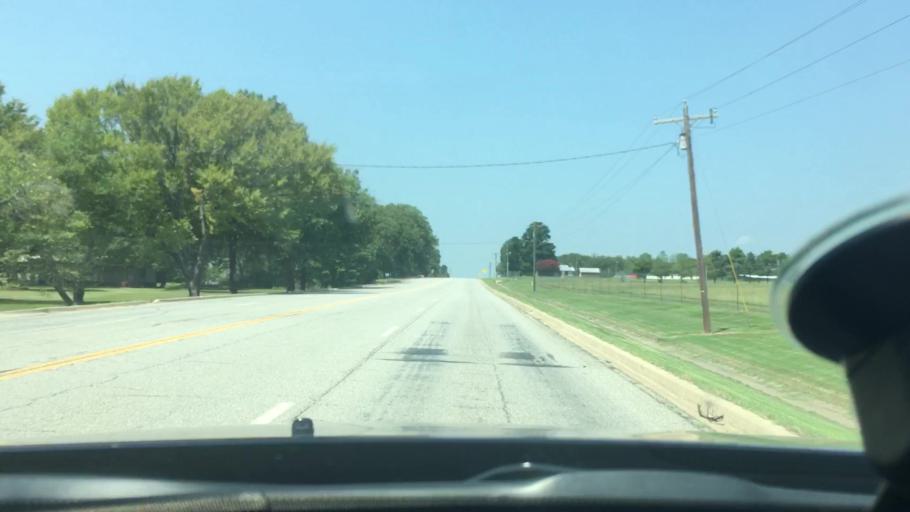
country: US
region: Oklahoma
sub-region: Atoka County
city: Atoka
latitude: 34.3041
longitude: -96.0011
